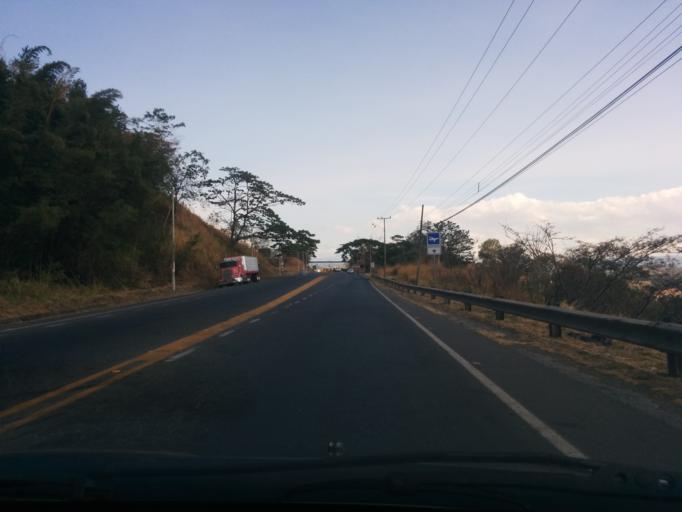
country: CR
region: Alajuela
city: Atenas
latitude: 10.0205
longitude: -84.3579
